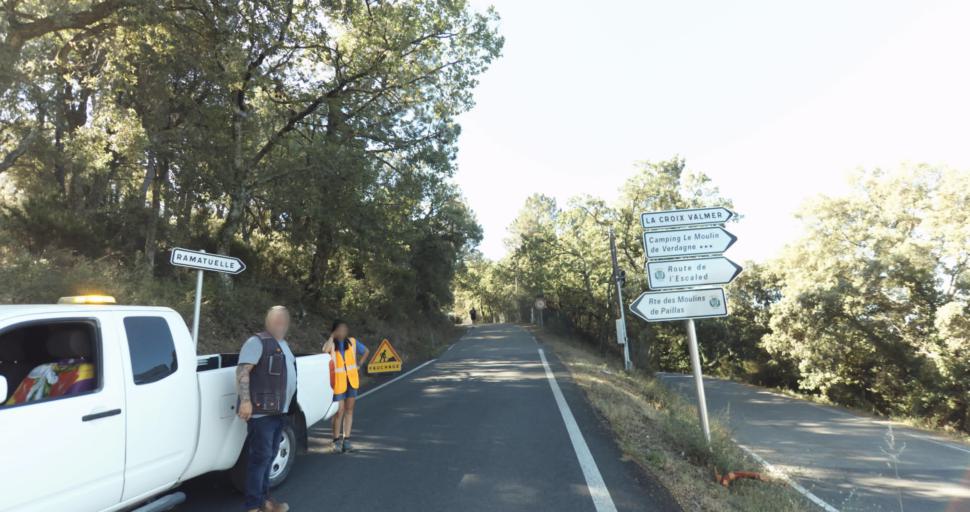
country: FR
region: Provence-Alpes-Cote d'Azur
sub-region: Departement du Var
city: Gassin
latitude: 43.2243
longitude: 6.5885
